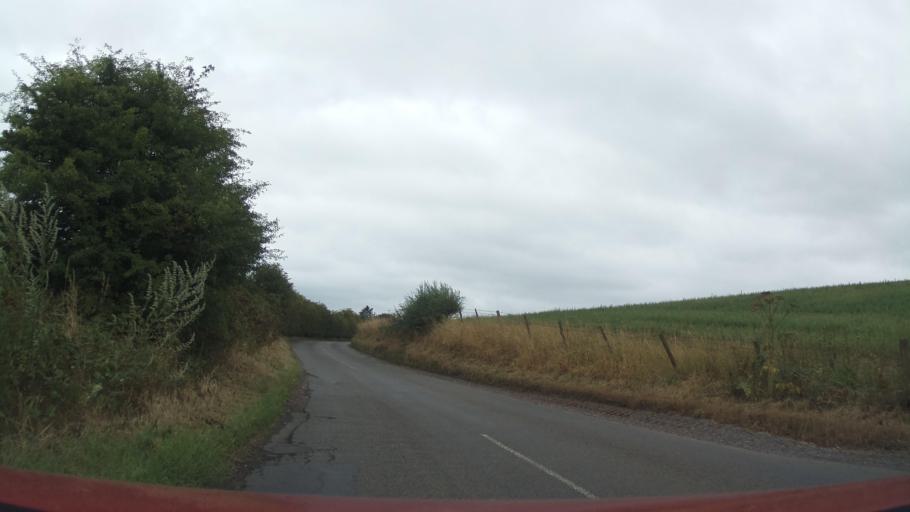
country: GB
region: England
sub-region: Derbyshire
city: Repton
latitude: 52.8125
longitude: -1.5454
